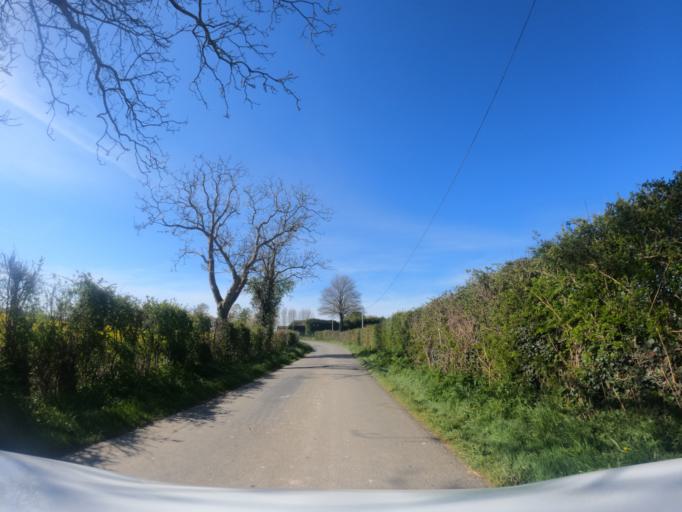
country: FR
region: Pays de la Loire
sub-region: Departement de la Vendee
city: La Tardiere
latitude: 46.6995
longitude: -0.7409
